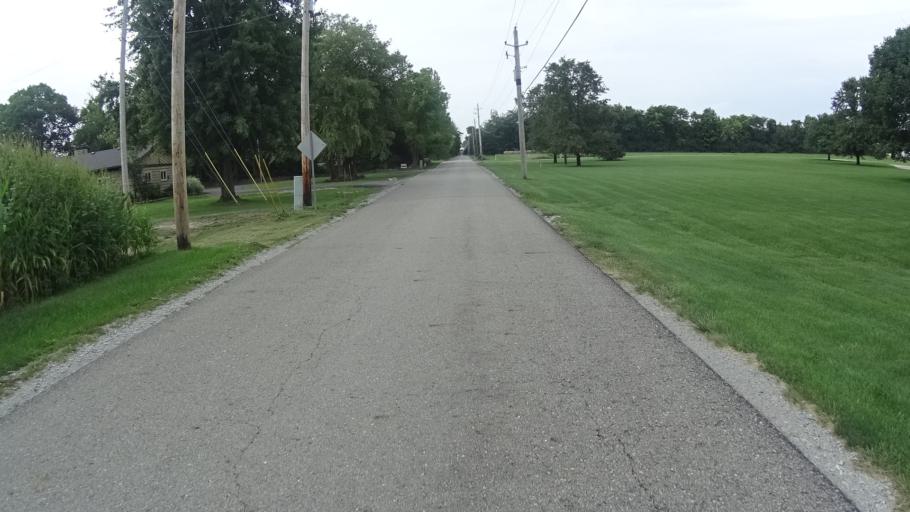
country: US
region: Indiana
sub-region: Madison County
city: Pendleton
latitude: 40.0078
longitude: -85.7870
